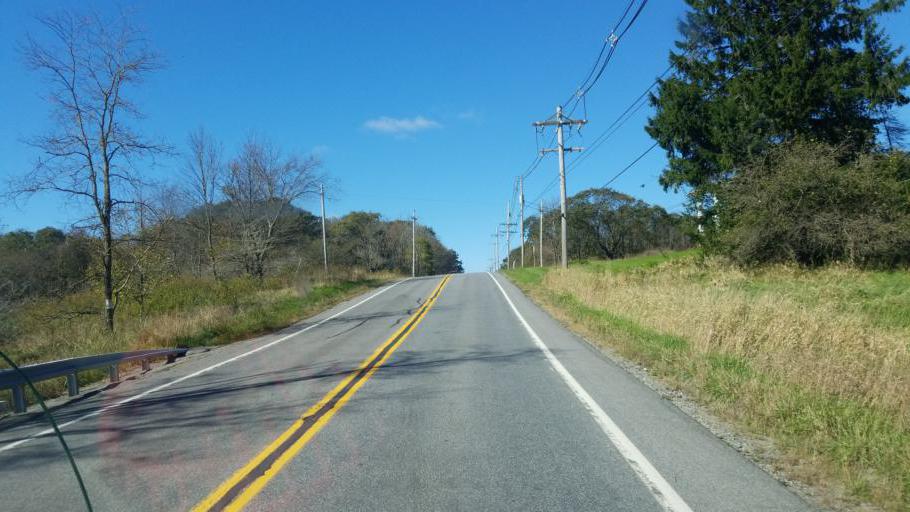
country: US
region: Pennsylvania
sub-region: Somerset County
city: Central City
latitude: 40.0520
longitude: -78.8117
